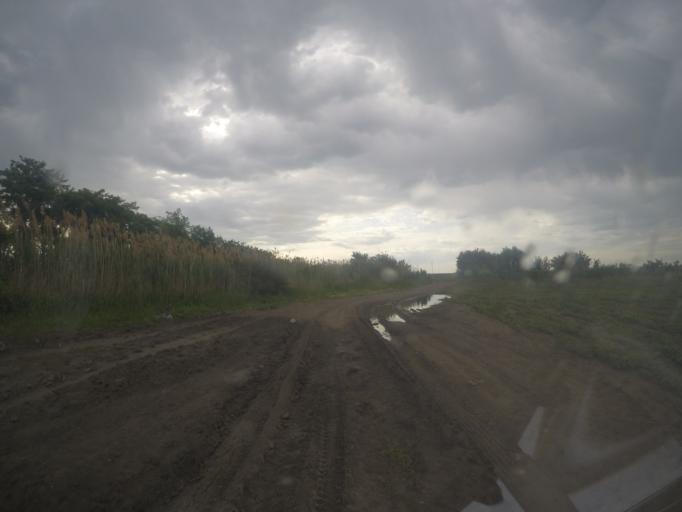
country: RS
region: Central Serbia
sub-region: Belgrade
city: Zemun
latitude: 44.8916
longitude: 20.4026
